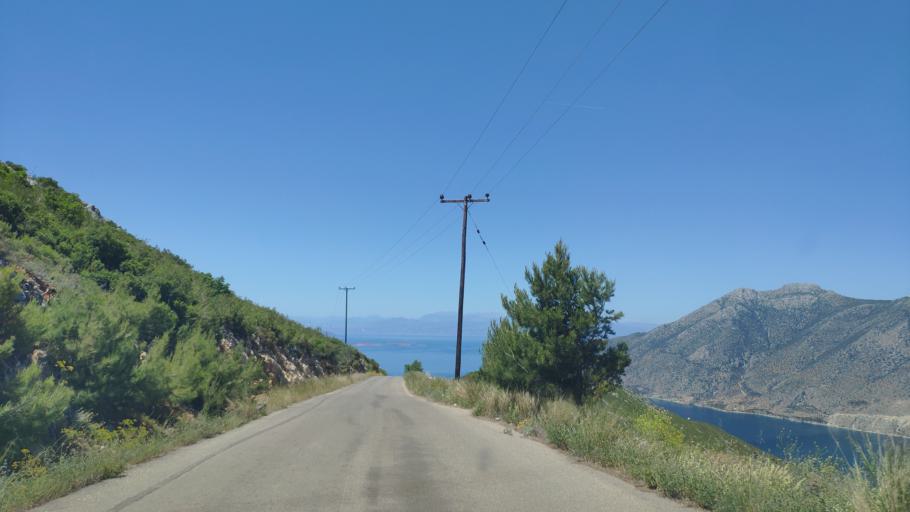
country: GR
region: Central Greece
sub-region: Nomos Voiotias
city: Kaparellion
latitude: 38.1977
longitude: 23.1482
